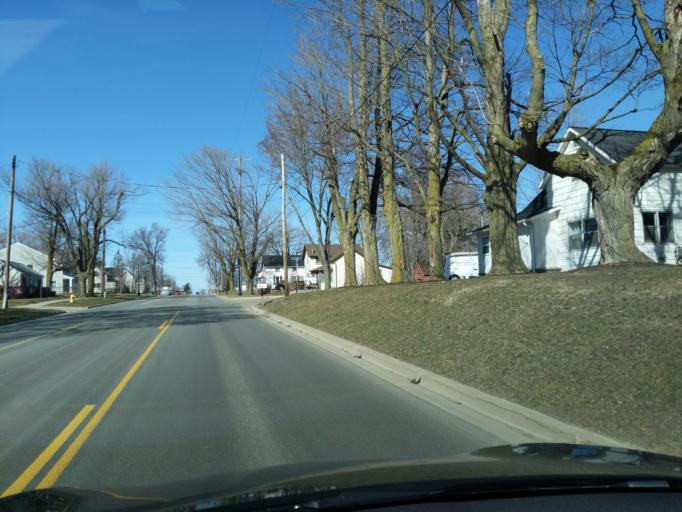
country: US
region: Michigan
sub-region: Ionia County
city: Lake Odessa
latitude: 42.7900
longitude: -85.1333
